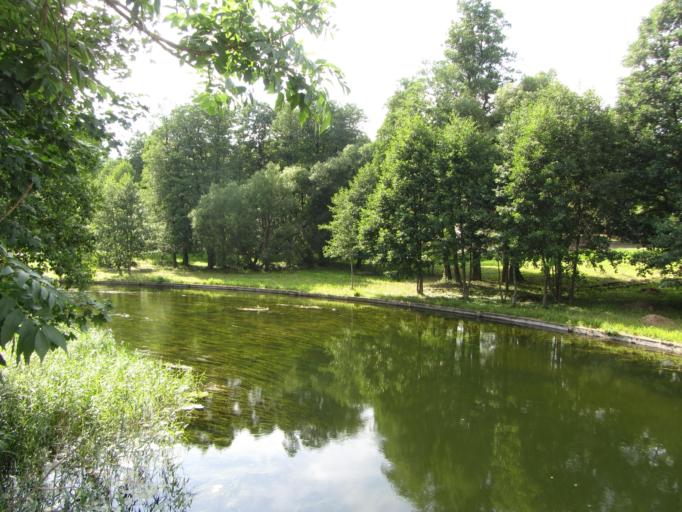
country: LT
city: Svencioneliai
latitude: 55.2533
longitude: 25.9919
